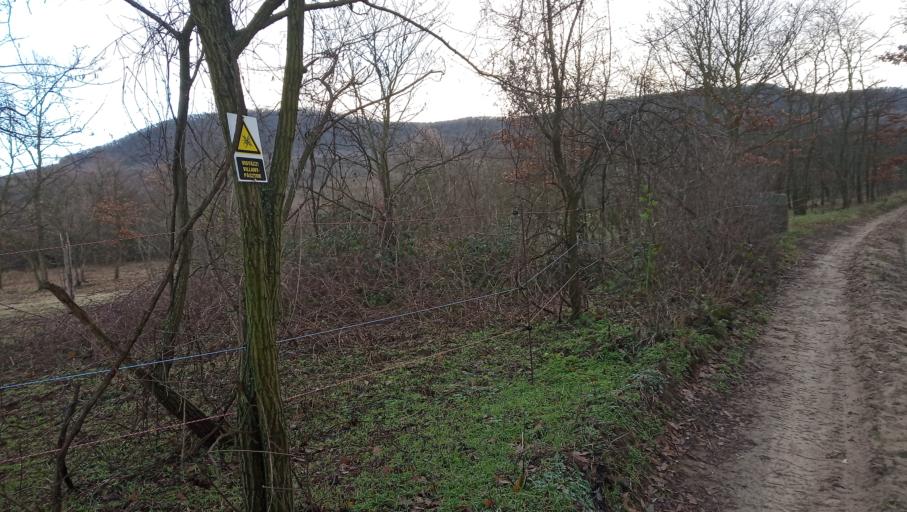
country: HU
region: Komarom-Esztergom
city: Piliscsev
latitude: 47.6694
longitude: 18.8250
